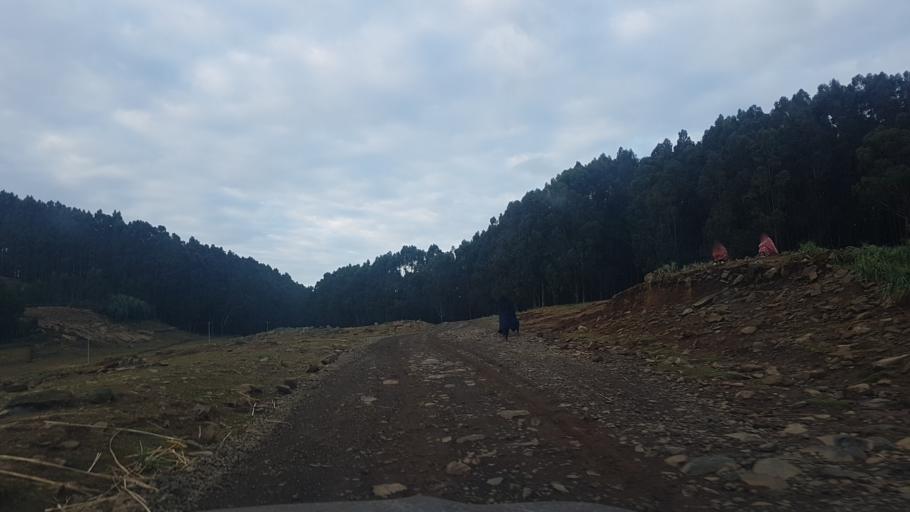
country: ET
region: Amhara
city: Finote Selam
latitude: 10.7974
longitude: 37.6630
